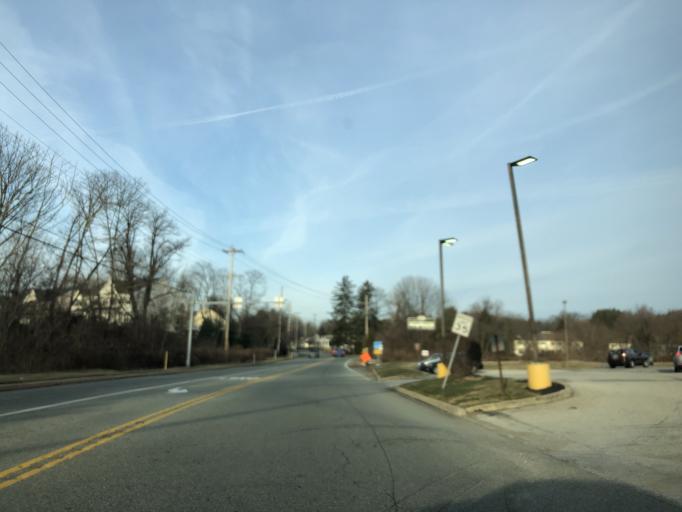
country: US
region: Pennsylvania
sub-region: Chester County
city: Exton
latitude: 40.0087
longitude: -75.5911
